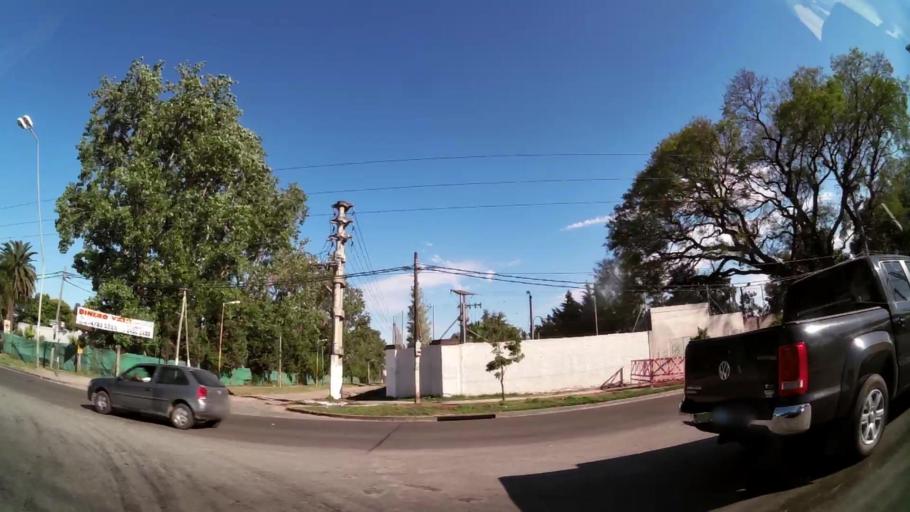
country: AR
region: Buenos Aires
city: Santa Catalina - Dique Lujan
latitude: -34.4826
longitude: -58.6812
